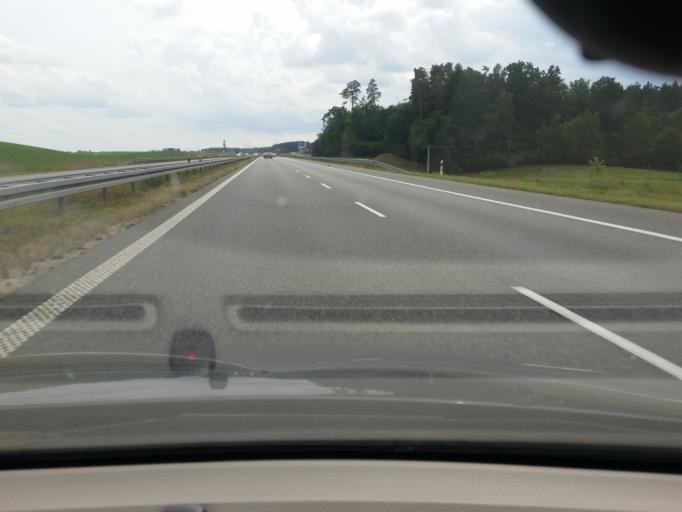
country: PL
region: Pomeranian Voivodeship
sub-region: Powiat tczewski
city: Pelplin
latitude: 53.8984
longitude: 18.6385
